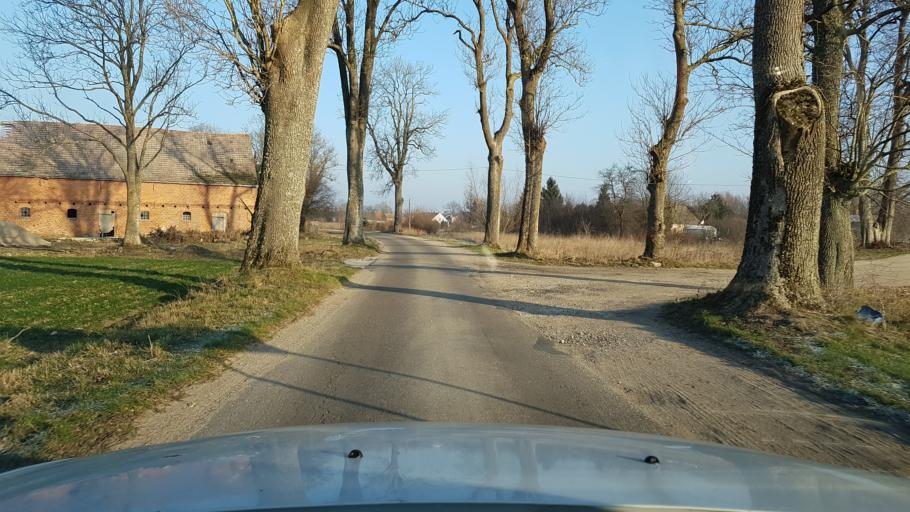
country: PL
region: West Pomeranian Voivodeship
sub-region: Powiat bialogardzki
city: Bialogard
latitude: 54.0686
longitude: 16.0866
